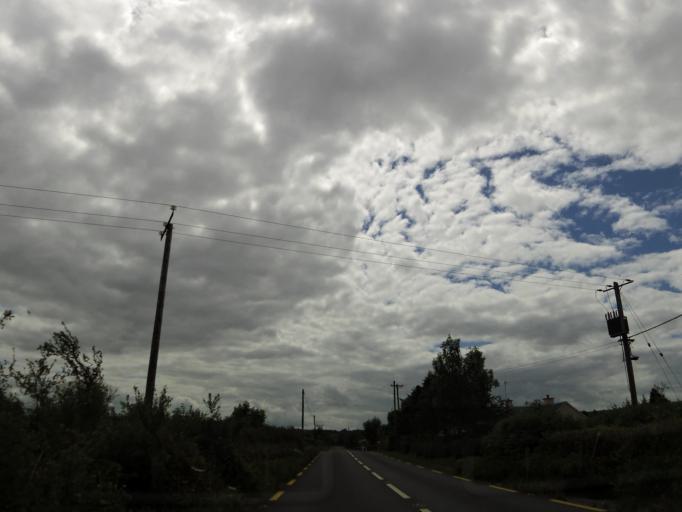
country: IE
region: Munster
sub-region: North Tipperary
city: Nenagh
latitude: 52.7844
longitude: -8.0339
